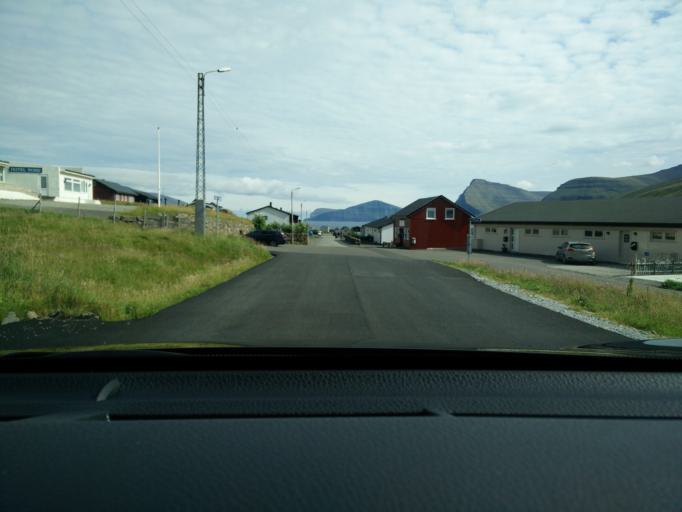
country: FO
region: Nordoyar
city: Klaksvik
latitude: 62.3603
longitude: -6.5319
